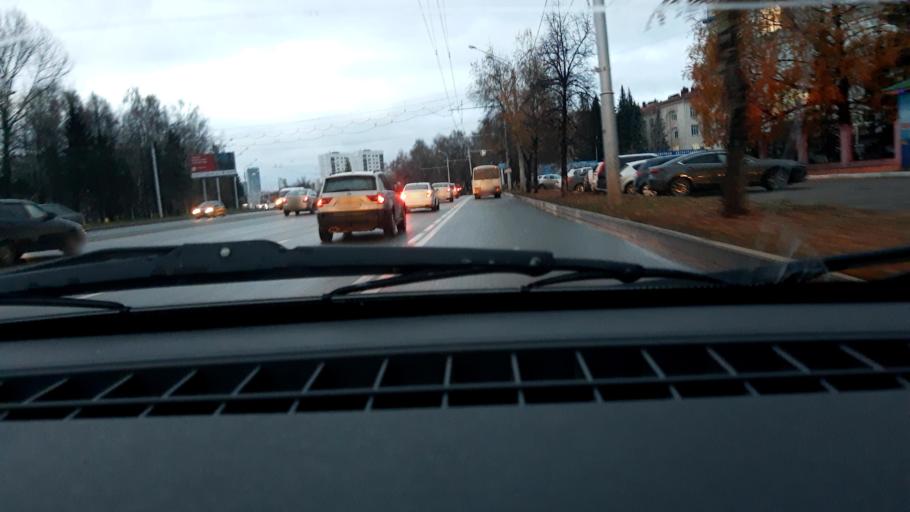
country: RU
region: Bashkortostan
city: Ufa
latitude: 54.7991
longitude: 56.0411
